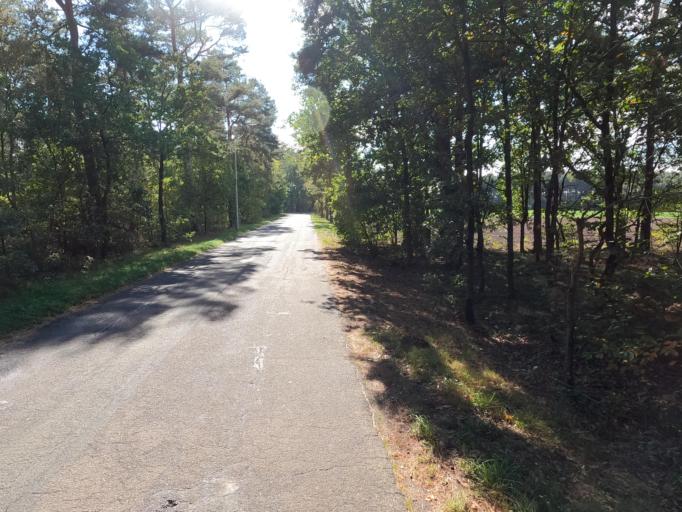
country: BE
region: Flanders
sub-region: Provincie Antwerpen
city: Lille
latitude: 51.2457
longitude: 4.8566
